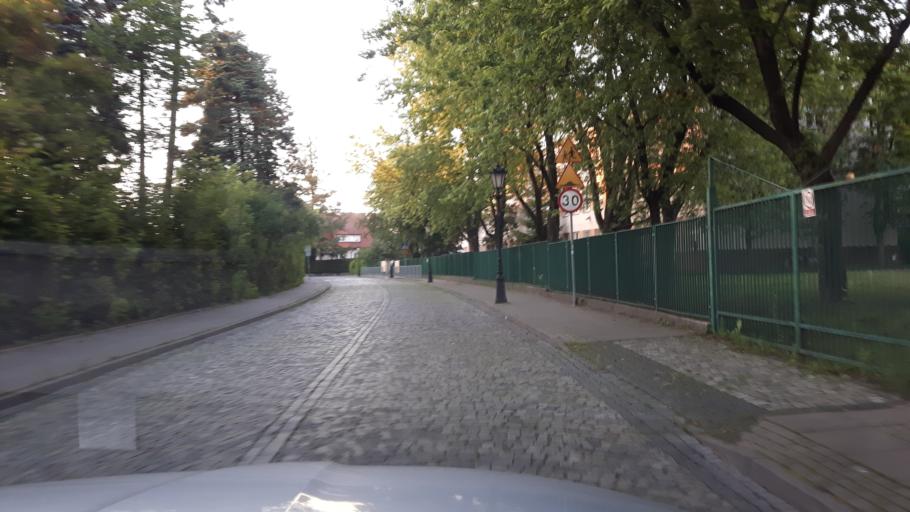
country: PL
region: Masovian Voivodeship
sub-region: Warszawa
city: Wilanow
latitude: 52.1871
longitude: 21.0702
